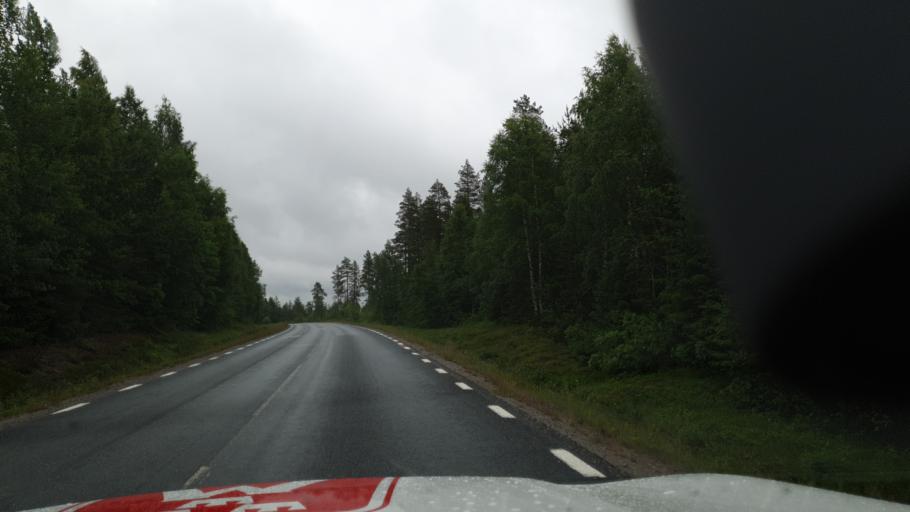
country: SE
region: Vaesterbotten
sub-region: Vannas Kommun
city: Vaennaes
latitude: 63.7724
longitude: 19.7182
